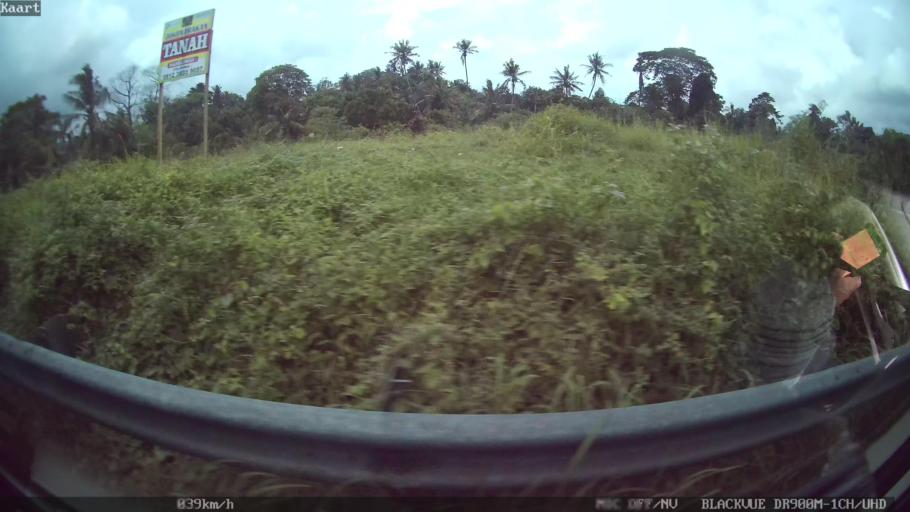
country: ID
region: Bali
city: Banjar Pekenjelodan
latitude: -8.5642
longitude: 115.1771
